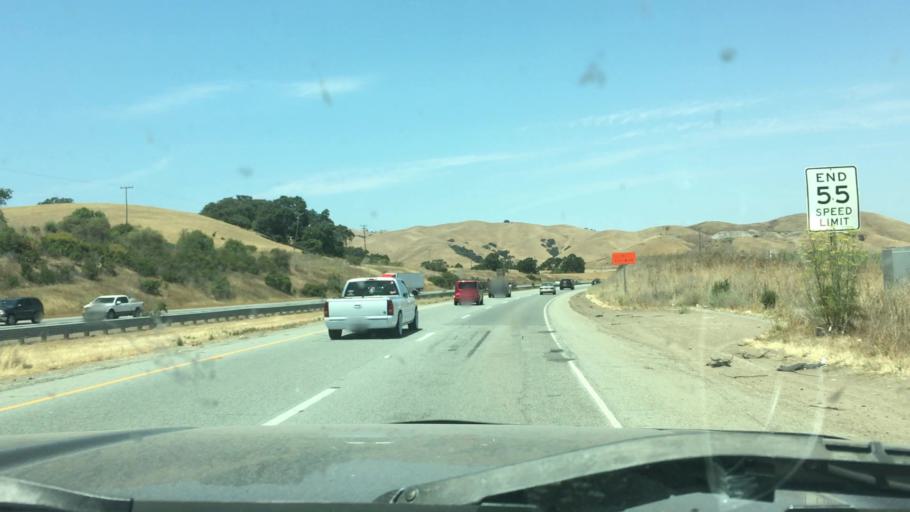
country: US
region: California
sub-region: Santa Clara County
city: Gilroy
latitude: 36.9828
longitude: -121.5530
